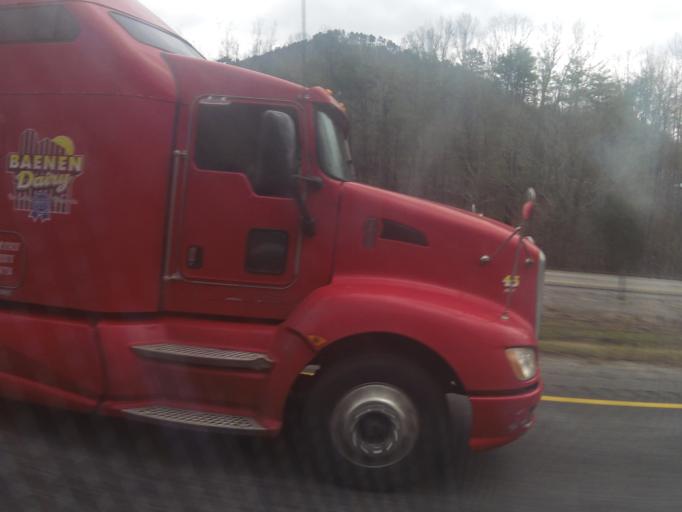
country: US
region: Georgia
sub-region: Dade County
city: Trenton
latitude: 34.9875
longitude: -85.5045
